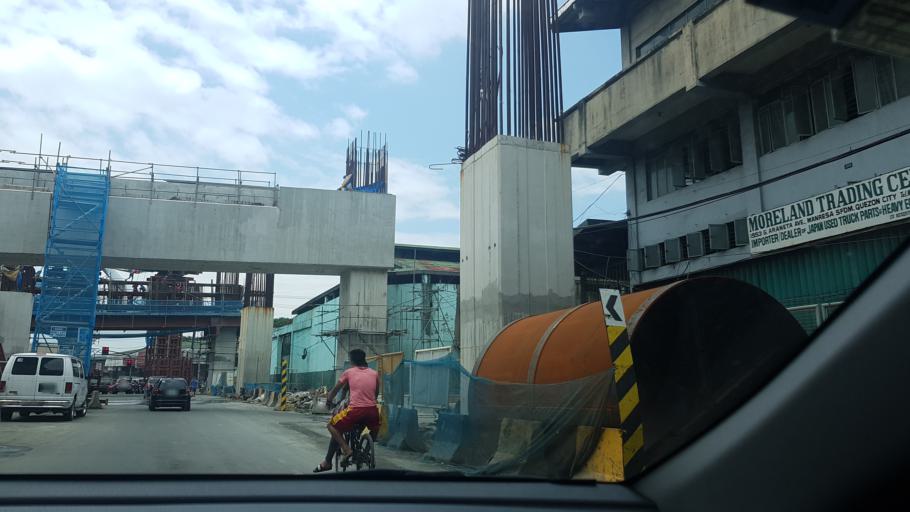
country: PH
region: Calabarzon
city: Del Monte
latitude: 14.6402
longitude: 121.0064
